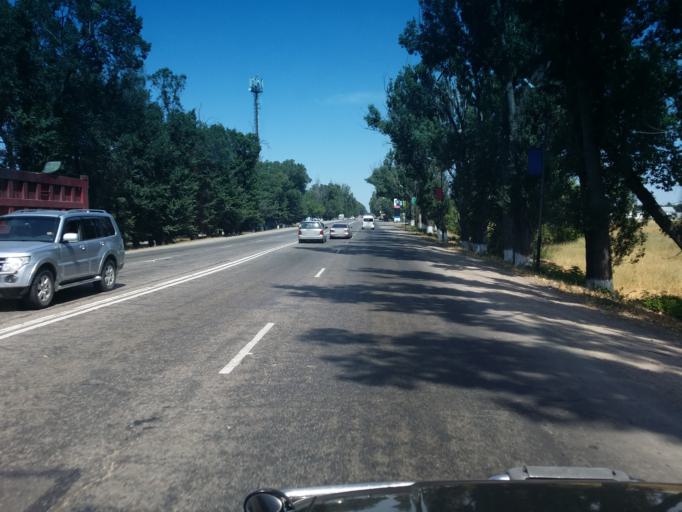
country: KZ
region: Almaty Oblysy
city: Energeticheskiy
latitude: 43.3487
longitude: 77.0600
